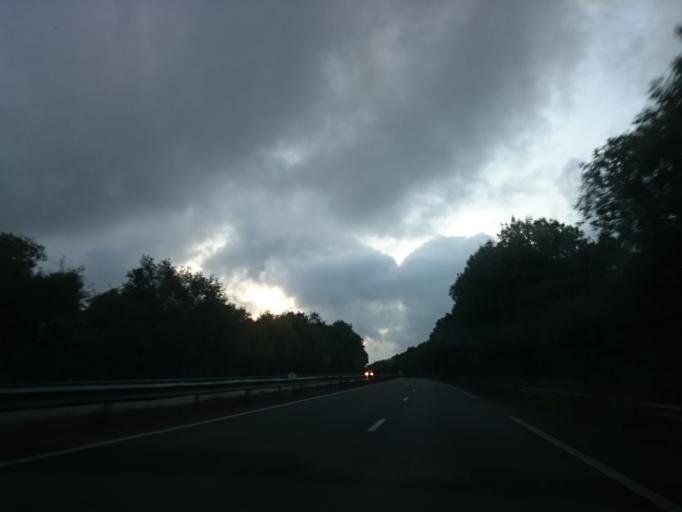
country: FR
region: Brittany
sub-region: Departement du Finistere
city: Melgven
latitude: 47.9161
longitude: -3.8741
